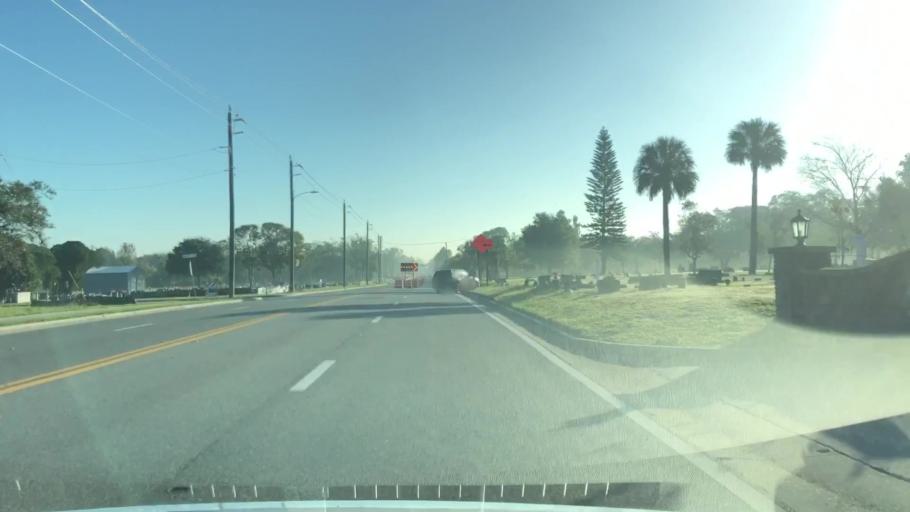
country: US
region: Florida
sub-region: Seminole County
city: Sanford
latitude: 28.7866
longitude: -81.2880
